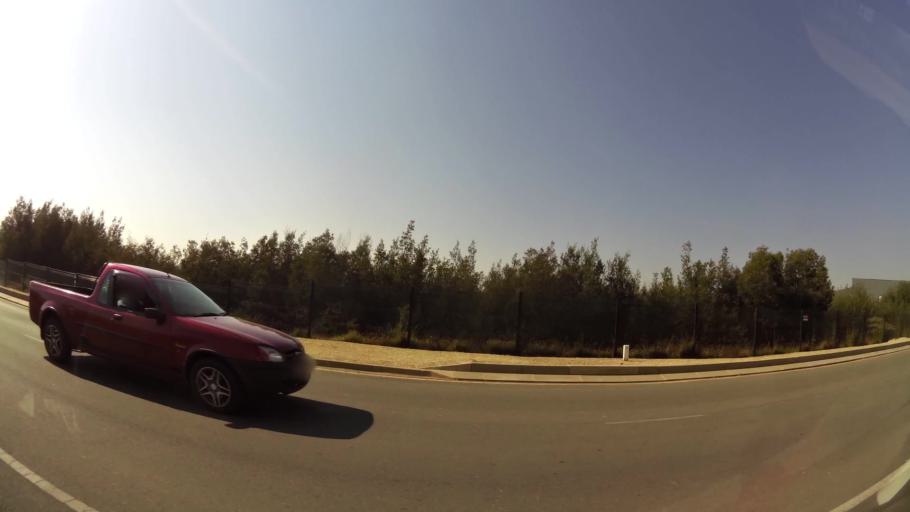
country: ZA
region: Gauteng
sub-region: City of Johannesburg Metropolitan Municipality
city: Modderfontein
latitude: -26.0978
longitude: 28.1403
